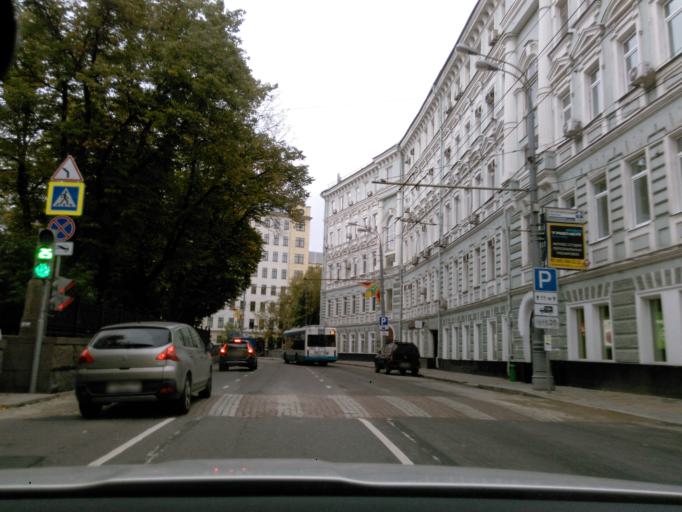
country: RU
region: Moscow
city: Moscow
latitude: 55.7472
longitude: 37.5994
